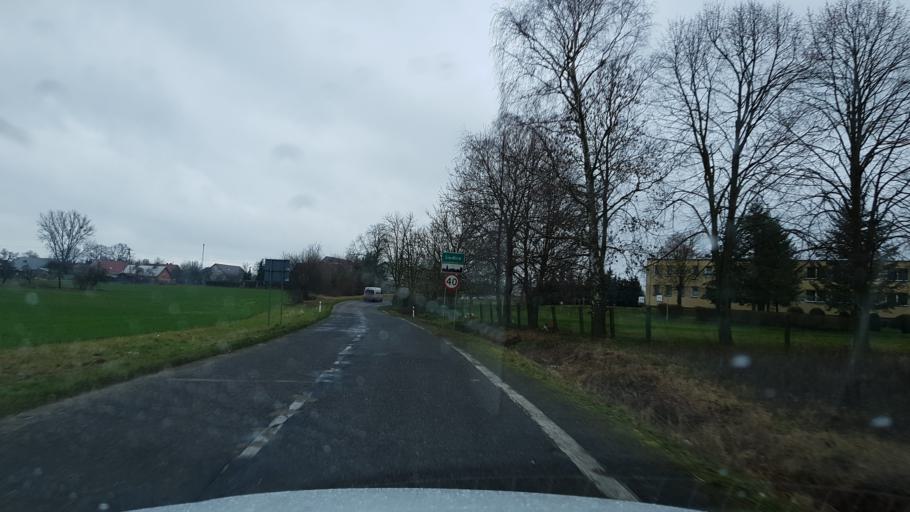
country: PL
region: West Pomeranian Voivodeship
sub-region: Powiat lobeski
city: Radowo Male
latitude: 53.6177
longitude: 15.4830
